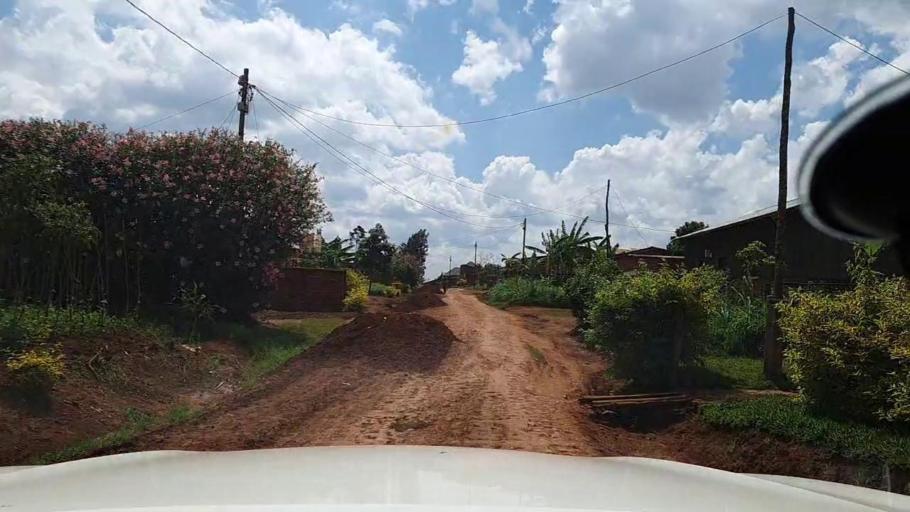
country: RW
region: Kigali
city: Kigali
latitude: -1.8339
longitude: 29.8360
